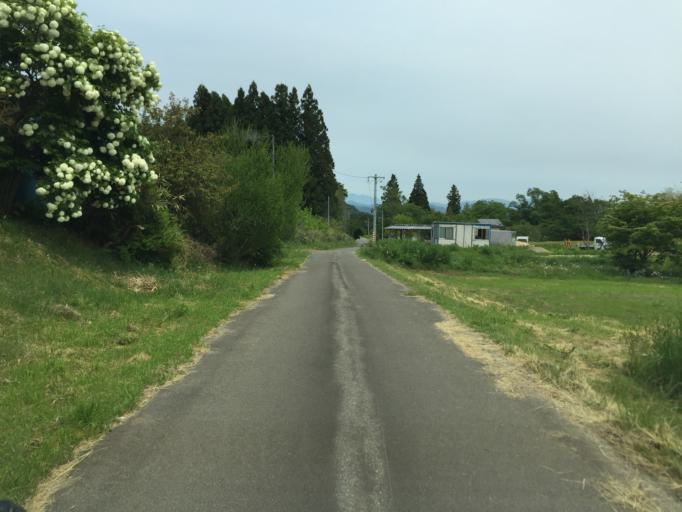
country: JP
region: Fukushima
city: Fukushima-shi
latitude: 37.7083
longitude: 140.3468
